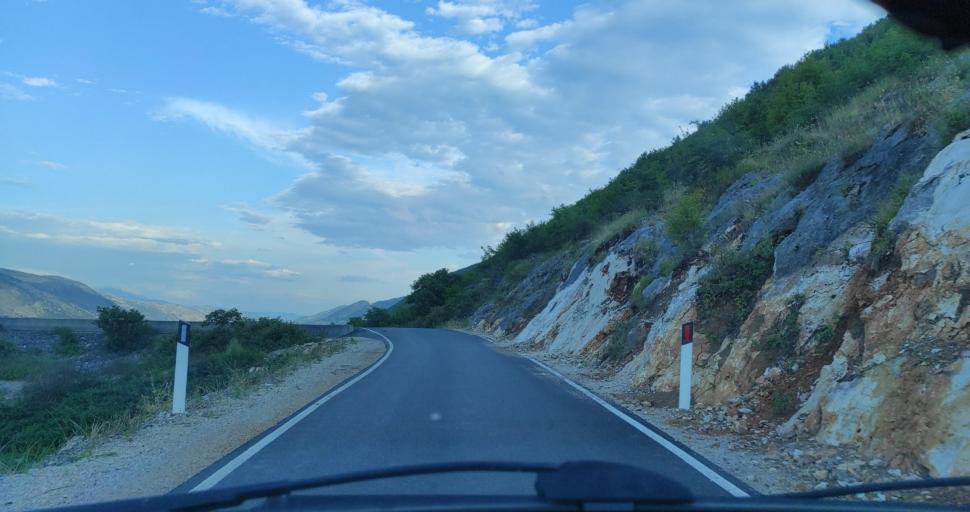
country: AL
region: Shkoder
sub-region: Rrethi i Shkodres
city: Velipoje
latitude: 41.9225
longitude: 19.4527
